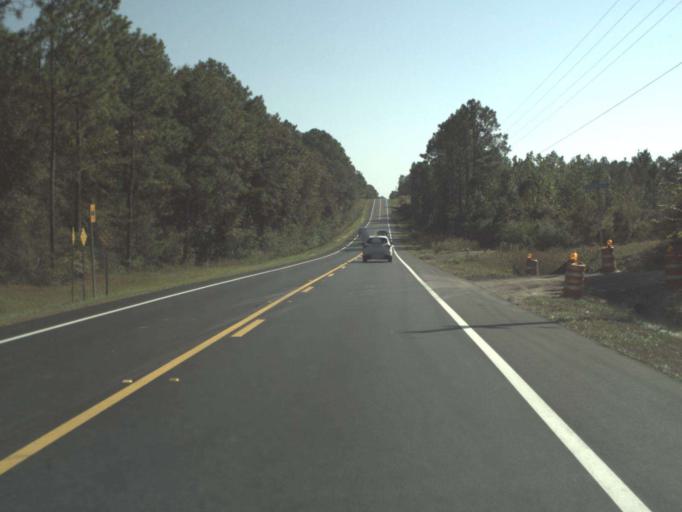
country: US
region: Alabama
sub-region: Covington County
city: Florala
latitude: 30.9121
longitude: -86.2812
